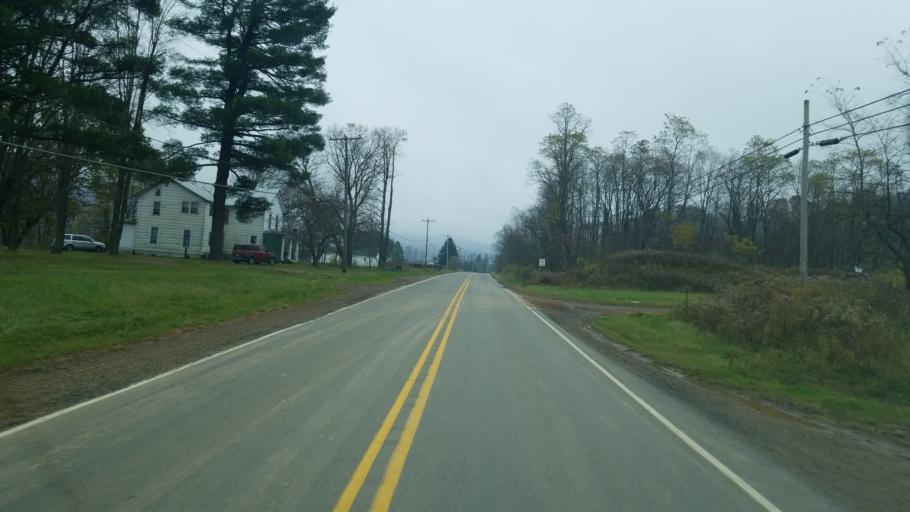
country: US
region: Pennsylvania
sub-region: McKean County
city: Smethport
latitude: 41.8435
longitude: -78.4399
